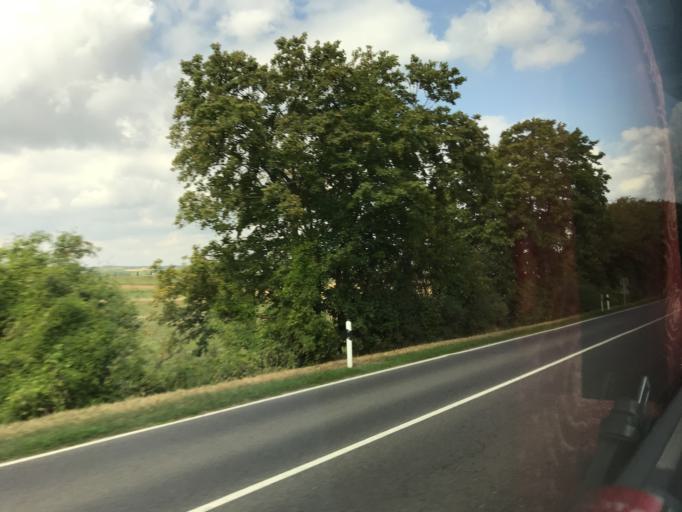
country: LU
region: Luxembourg
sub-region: Canton de Luxembourg
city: Alzingen
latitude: 49.5484
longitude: 6.1738
